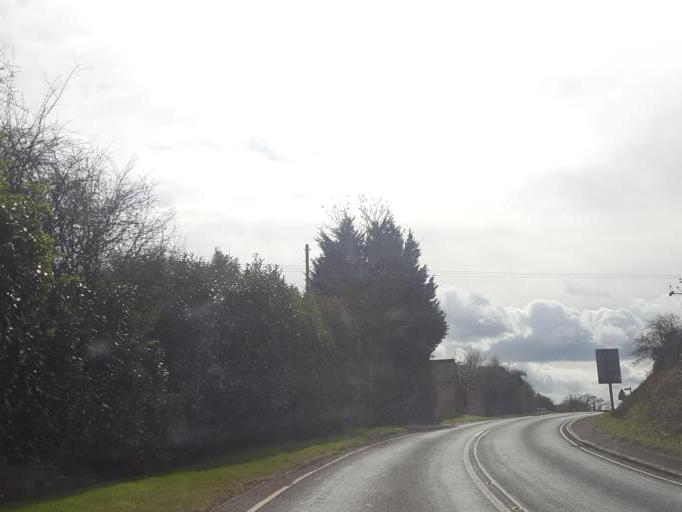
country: GB
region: England
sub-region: Worcestershire
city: Bransford
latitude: 52.1705
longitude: -2.3006
